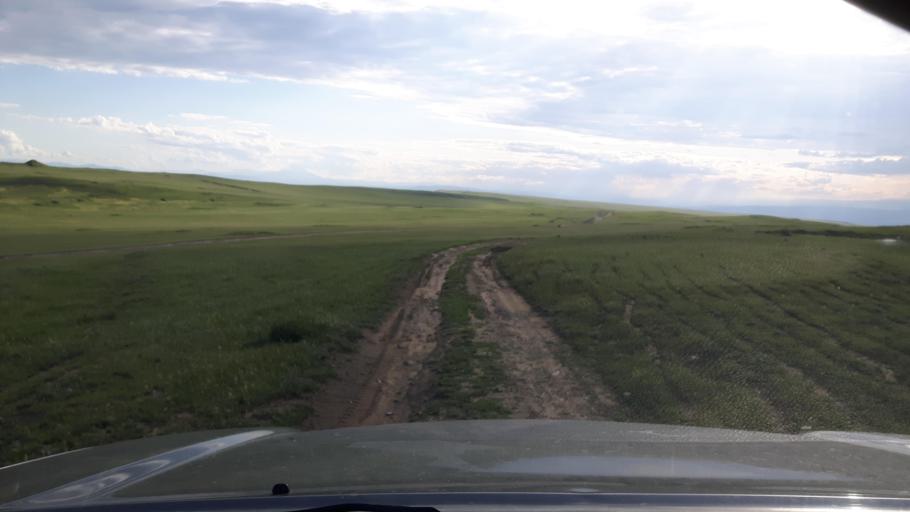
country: AZ
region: Agstafa
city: Saloglu
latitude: 41.4746
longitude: 45.3010
